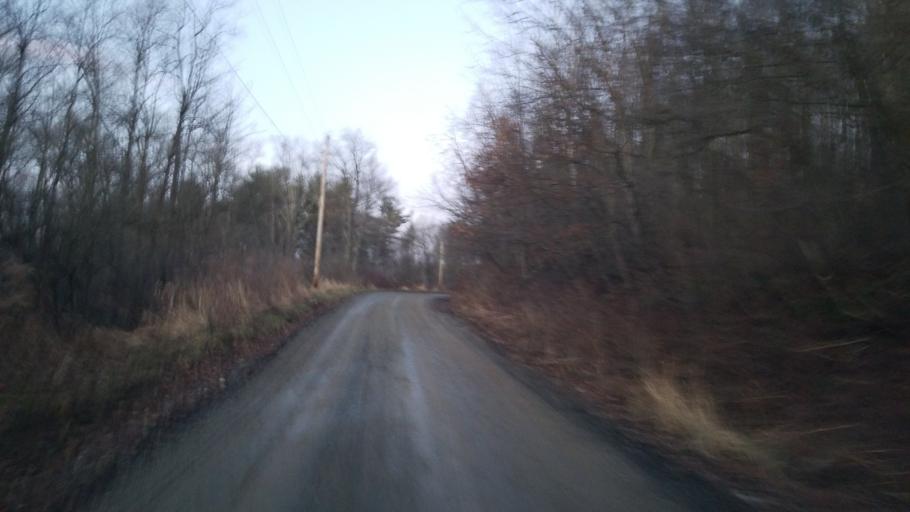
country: US
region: Pennsylvania
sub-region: Indiana County
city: Chevy Chase Heights
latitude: 40.8442
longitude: -79.1689
